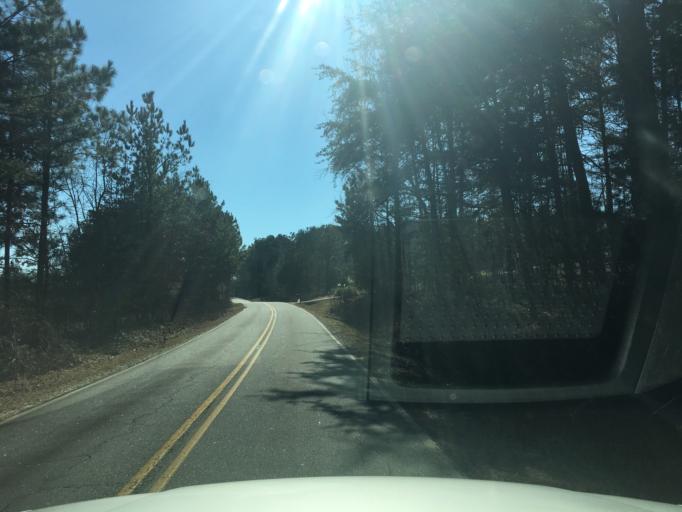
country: US
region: South Carolina
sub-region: Pickens County
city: Pickens
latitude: 34.8321
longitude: -82.7869
